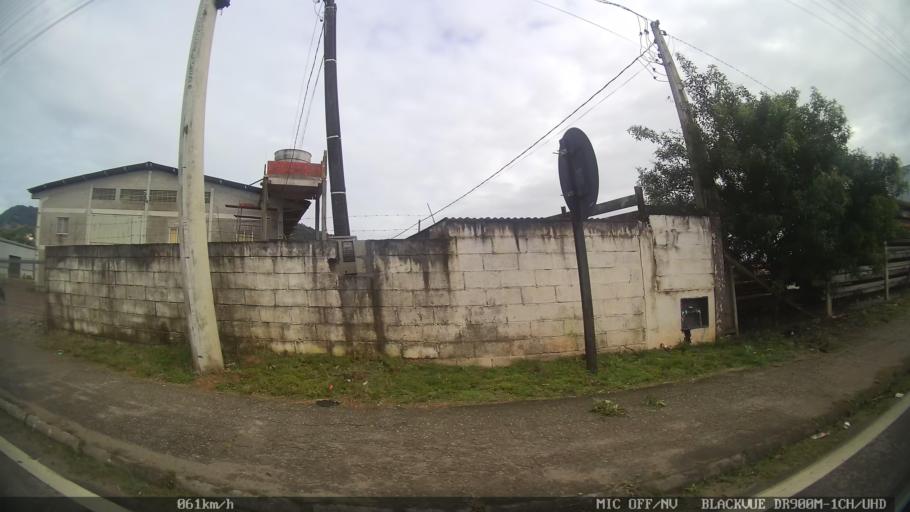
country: BR
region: Santa Catarina
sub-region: Biguacu
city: Biguacu
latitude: -27.4959
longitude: -48.6575
